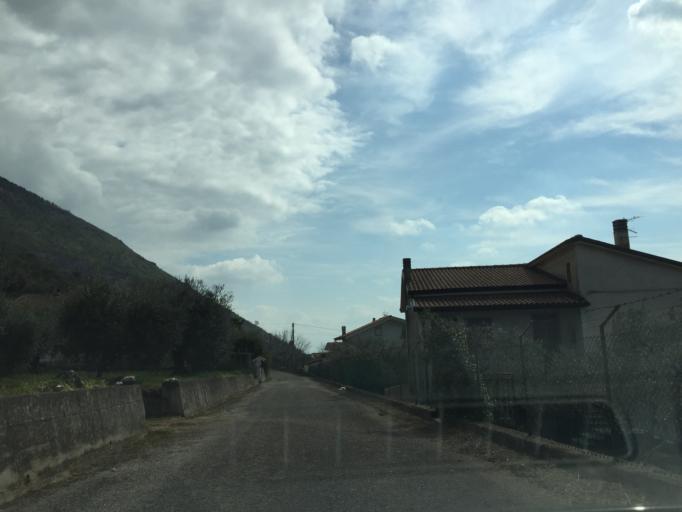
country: IT
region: Latium
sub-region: Provincia di Frosinone
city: Castrocielo
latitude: 41.5292
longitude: 13.6994
